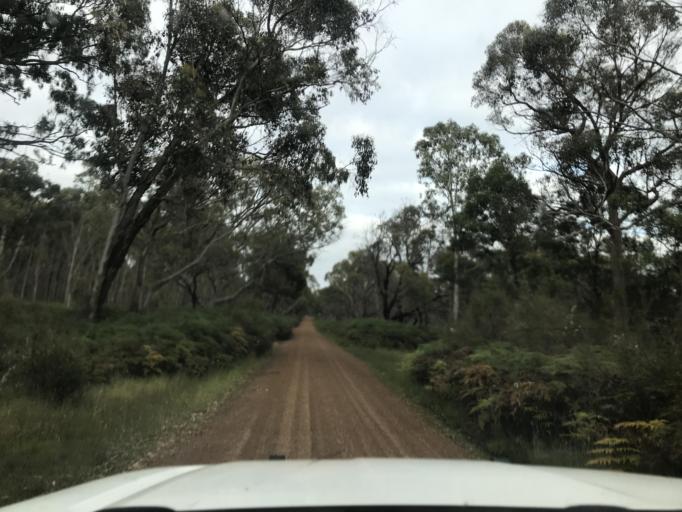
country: AU
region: South Australia
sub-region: Wattle Range
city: Penola
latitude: -37.2795
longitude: 141.3862
